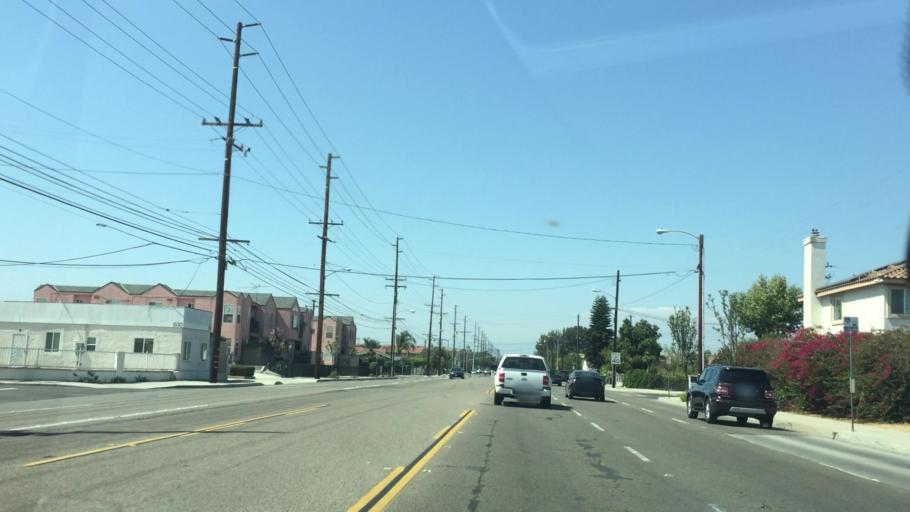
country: US
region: California
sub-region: Orange County
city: Garden Grove
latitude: 33.7490
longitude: -117.9375
